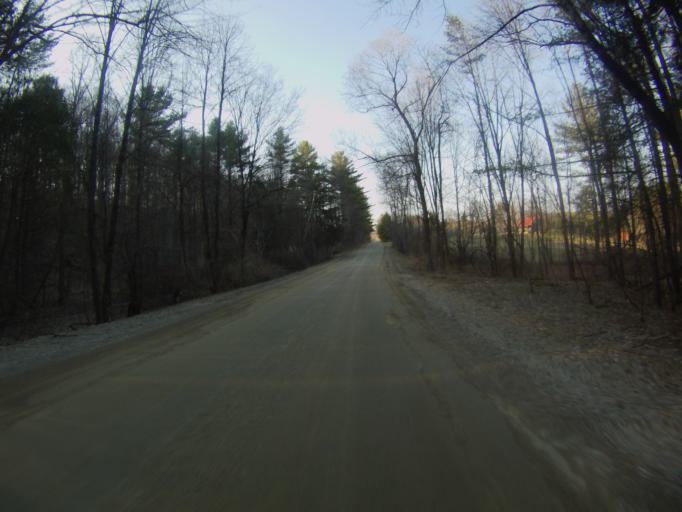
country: US
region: Vermont
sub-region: Addison County
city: Middlebury (village)
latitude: 44.0526
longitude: -73.1463
